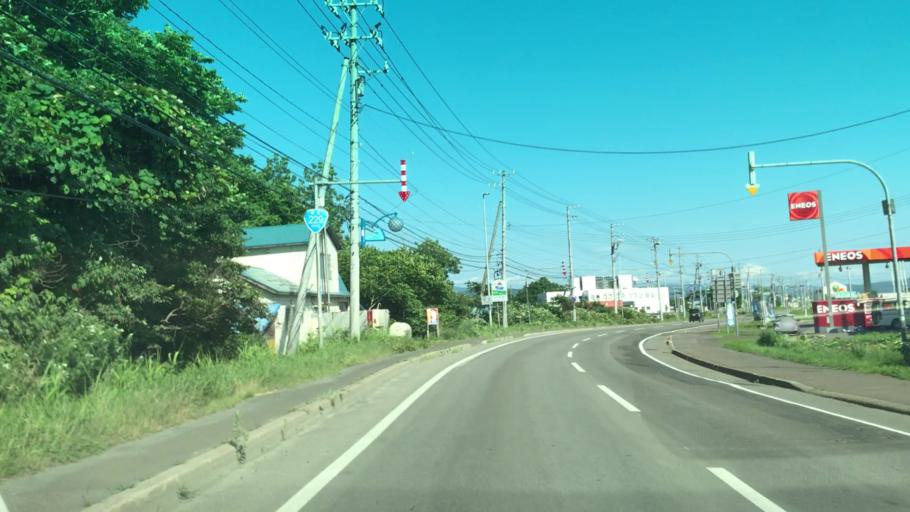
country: JP
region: Hokkaido
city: Iwanai
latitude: 43.0329
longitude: 140.5334
